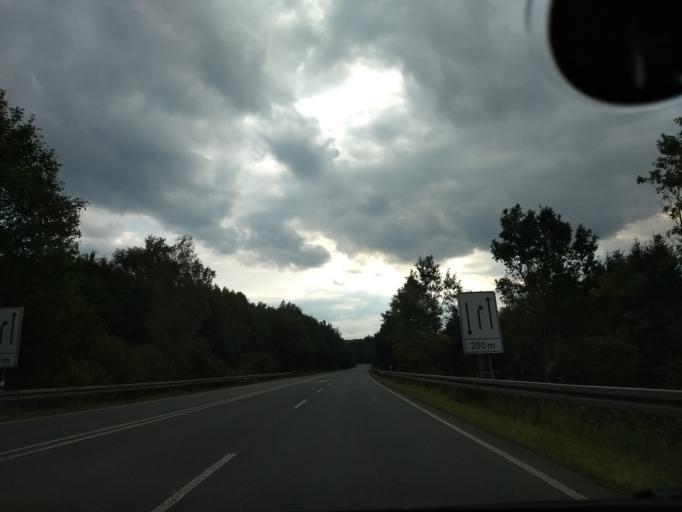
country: DE
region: North Rhine-Westphalia
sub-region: Regierungsbezirk Arnsberg
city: Ruthen
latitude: 51.5006
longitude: 8.4524
